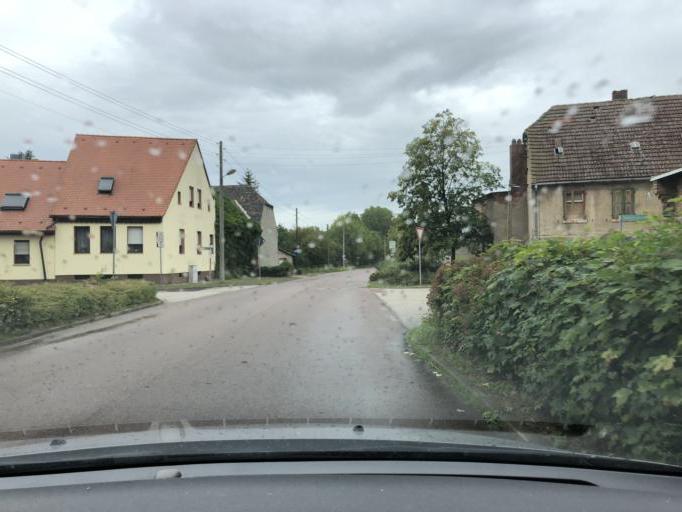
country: DE
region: Saxony-Anhalt
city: Wulfen
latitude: 51.8173
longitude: 11.9068
